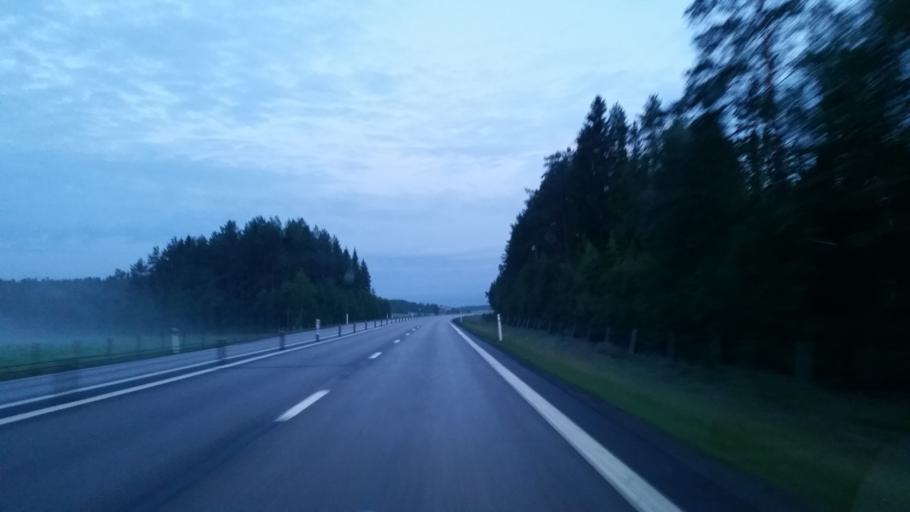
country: SE
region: Vaesterbotten
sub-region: Robertsfors Kommun
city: Robertsfors
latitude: 64.1151
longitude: 20.8806
